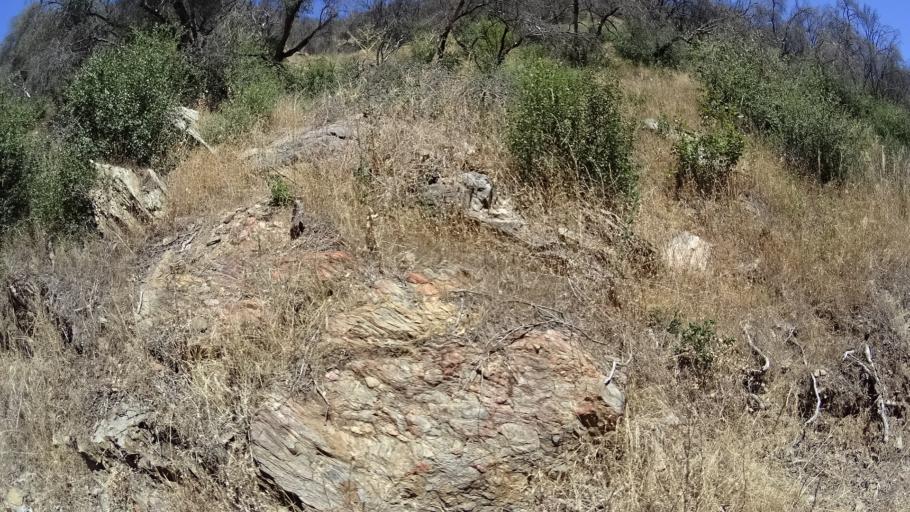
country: US
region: California
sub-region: Calaveras County
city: San Andreas
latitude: 38.2849
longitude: -120.6555
